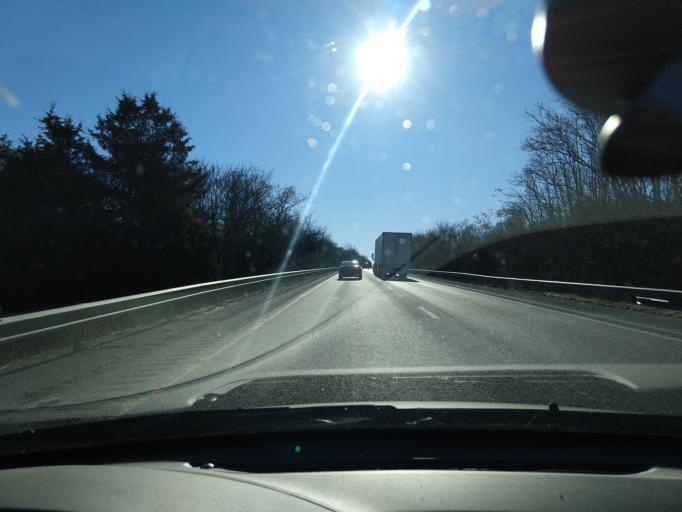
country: US
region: Virginia
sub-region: City of Lexington
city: Lexington
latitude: 37.7279
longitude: -79.4330
